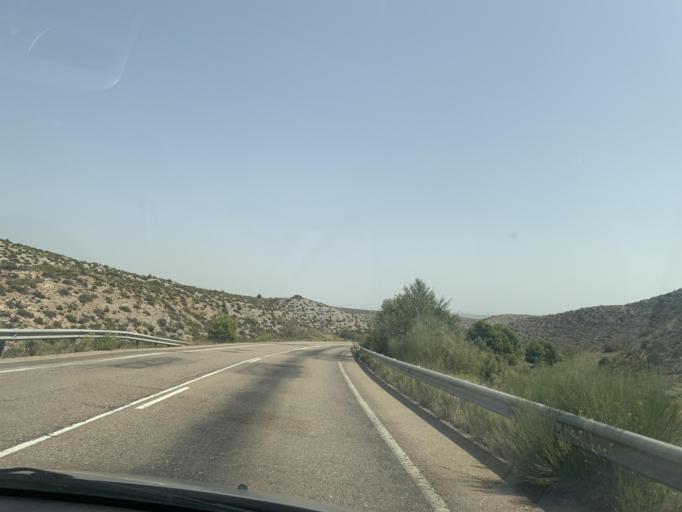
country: ES
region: Aragon
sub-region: Provincia de Zaragoza
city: El Burgo de Ebro
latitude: 41.5256
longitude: -0.7030
